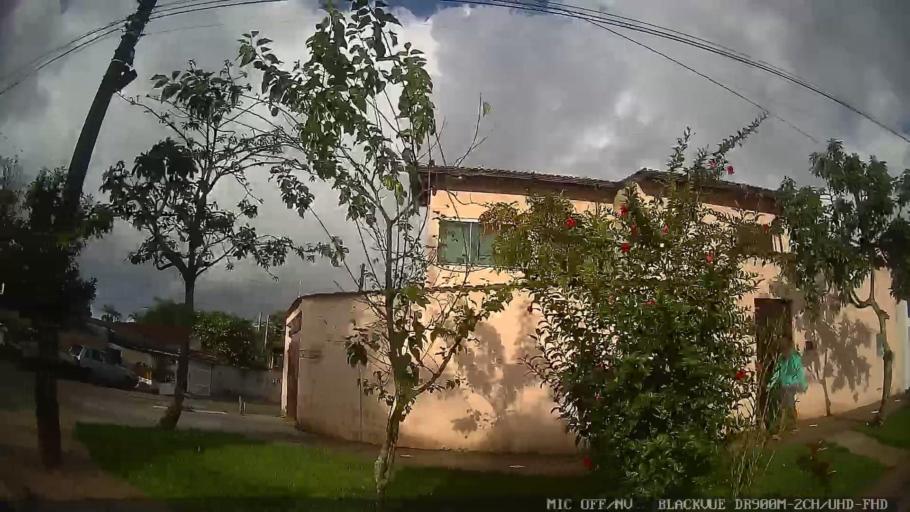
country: BR
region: Sao Paulo
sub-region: Itanhaem
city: Itanhaem
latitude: -24.2013
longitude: -46.8712
